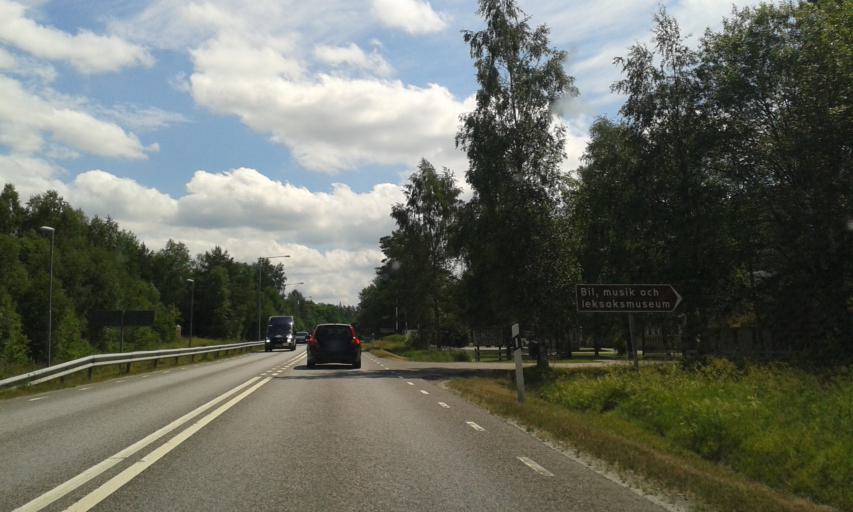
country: SE
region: Joenkoeping
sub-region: Varnamo Kommun
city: Rydaholm
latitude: 56.9719
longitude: 14.3256
